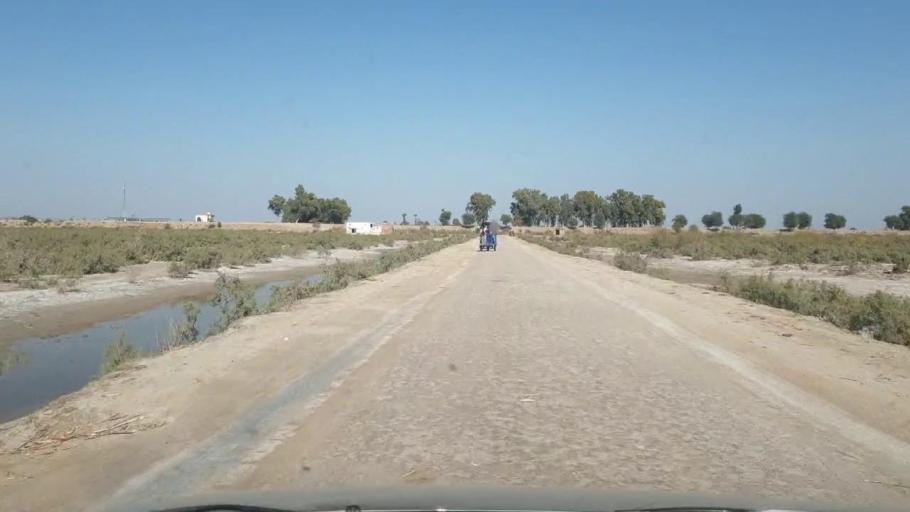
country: PK
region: Sindh
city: Samaro
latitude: 25.3738
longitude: 69.3283
